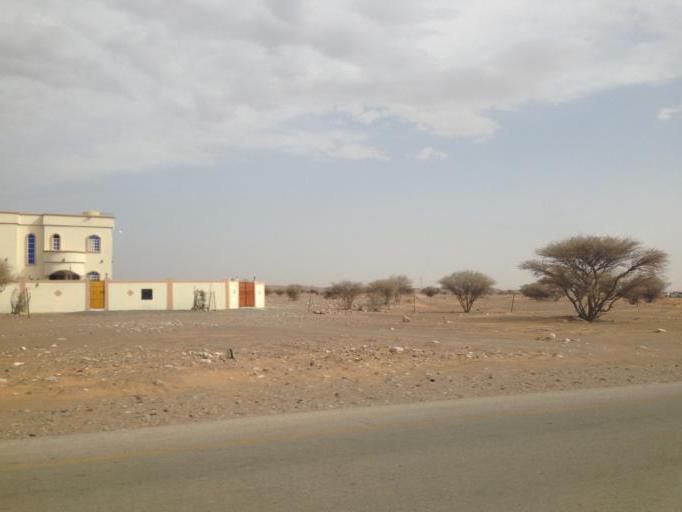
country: OM
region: Ash Sharqiyah
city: Badiyah
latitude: 22.5015
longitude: 58.9438
